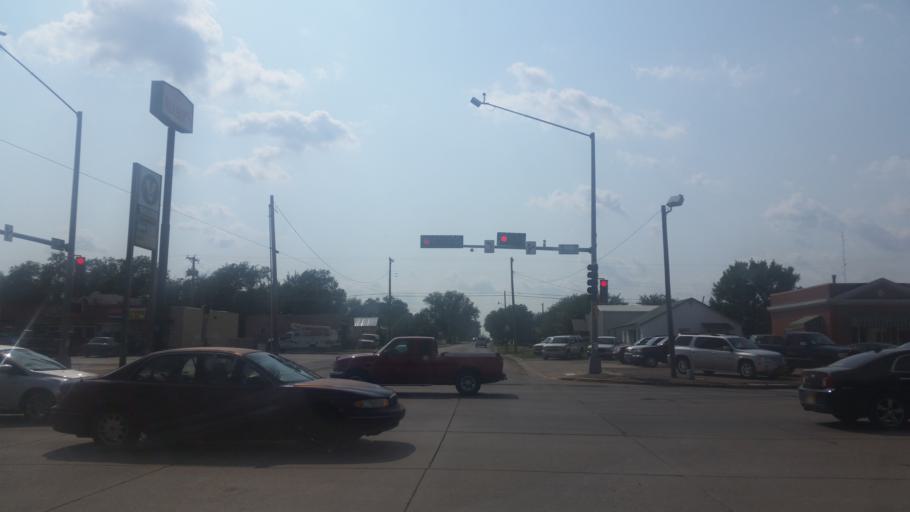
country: US
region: New Mexico
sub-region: Curry County
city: Clovis
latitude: 34.4121
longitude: -103.1963
